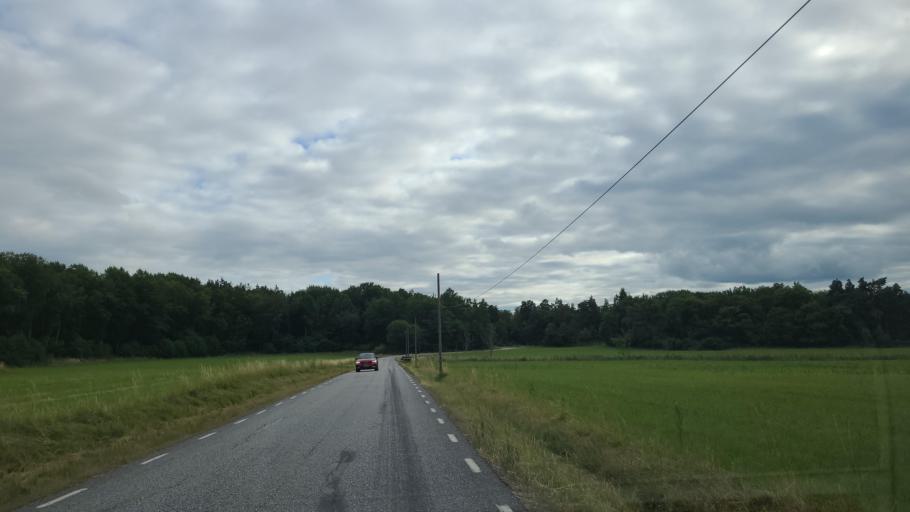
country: SE
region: Stockholm
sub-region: Upplands-Bro Kommun
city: Bro
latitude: 59.4736
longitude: 17.5952
